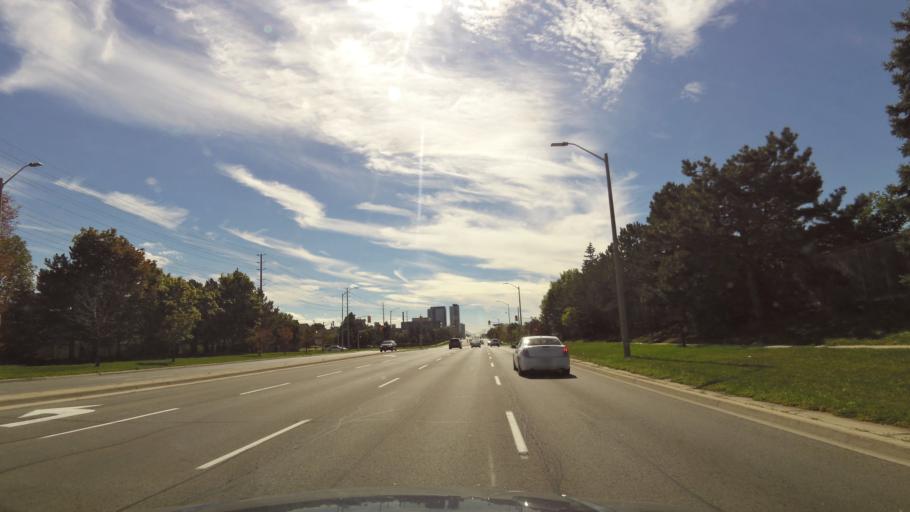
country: CA
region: Ontario
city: Mississauga
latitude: 43.5662
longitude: -79.6987
